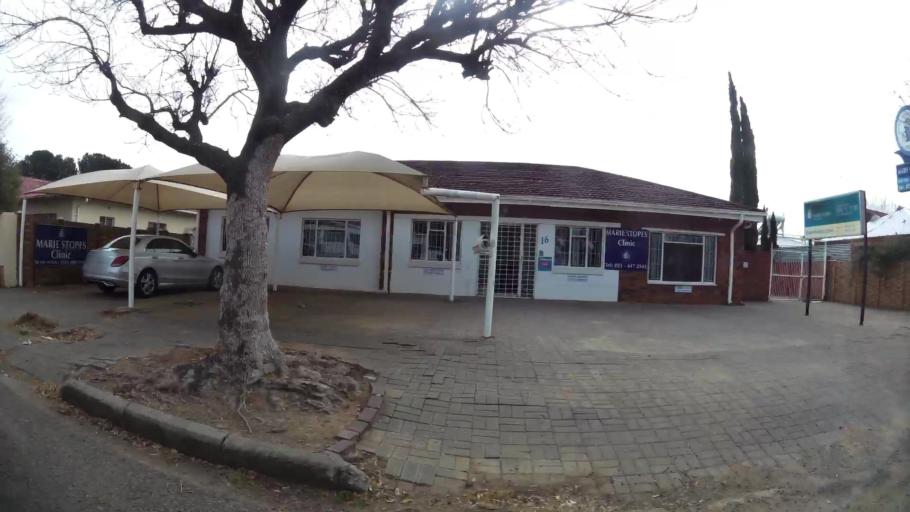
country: ZA
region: Orange Free State
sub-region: Mangaung Metropolitan Municipality
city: Bloemfontein
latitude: -29.1261
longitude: 26.2075
